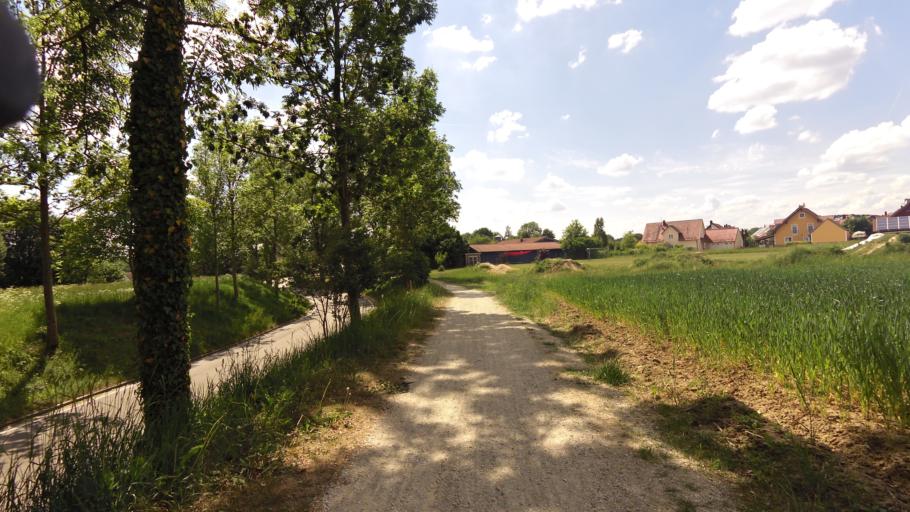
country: DE
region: Bavaria
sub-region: Upper Bavaria
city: Wang
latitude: 48.4970
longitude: 11.9404
